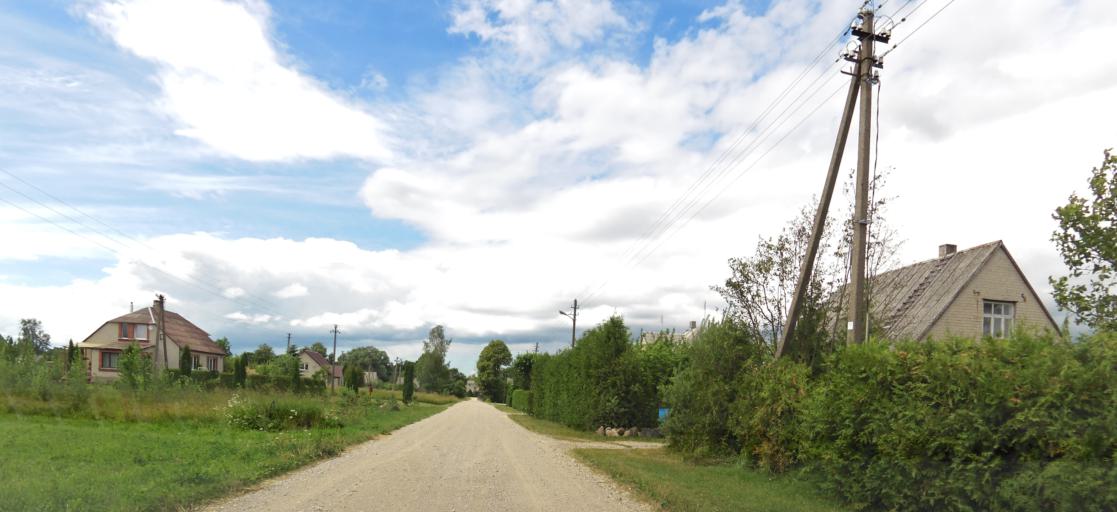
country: LT
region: Panevezys
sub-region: Birzai
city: Birzai
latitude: 56.3927
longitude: 24.7742
